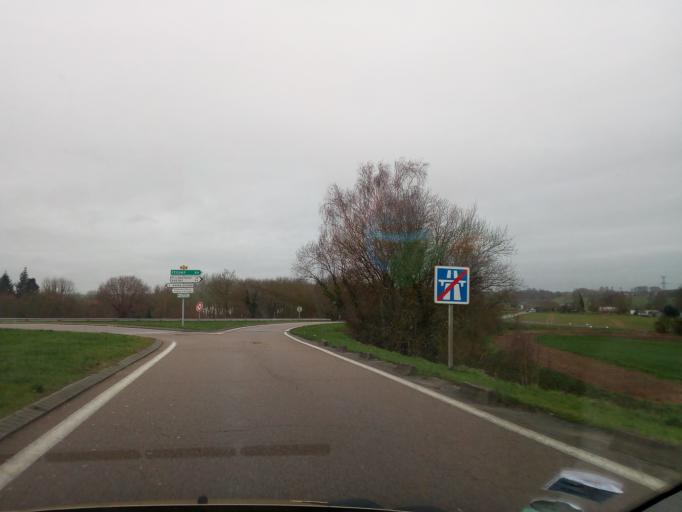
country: FR
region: Haute-Normandie
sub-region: Departement de l'Eure
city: Bourg-Achard
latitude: 49.3673
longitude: 0.8151
